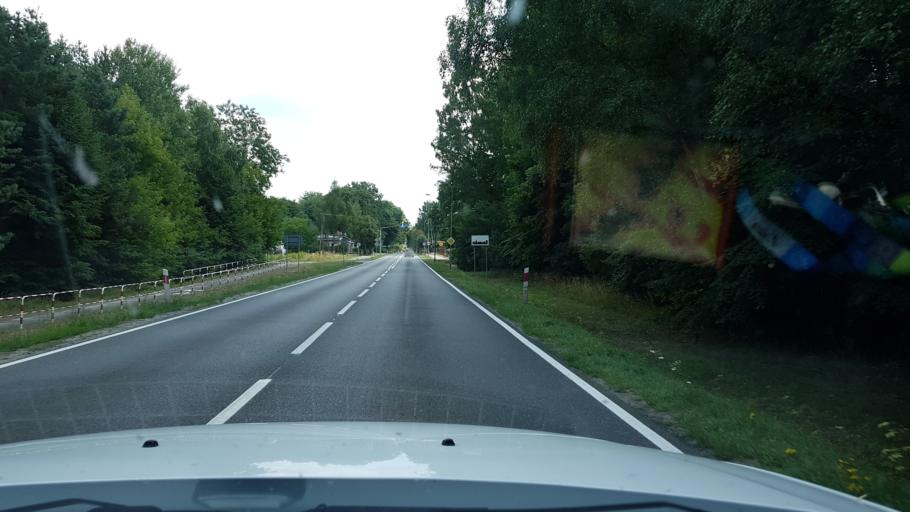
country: PL
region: West Pomeranian Voivodeship
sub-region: Powiat walecki
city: Walcz
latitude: 53.2910
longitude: 16.4332
